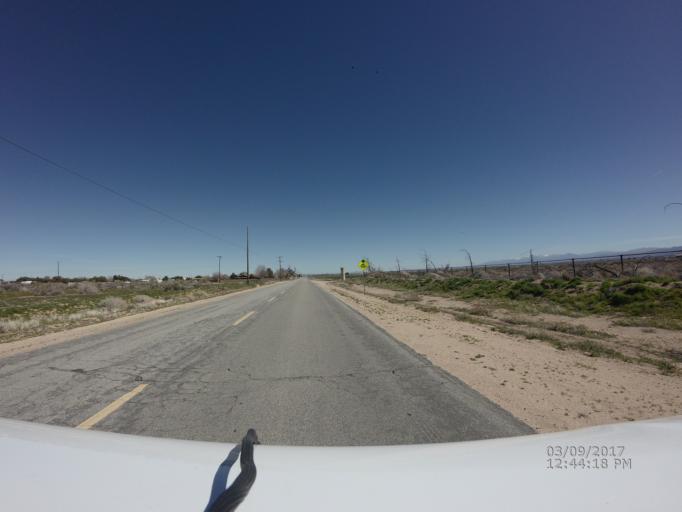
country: US
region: California
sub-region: Los Angeles County
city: Quartz Hill
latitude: 34.7474
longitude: -118.2821
